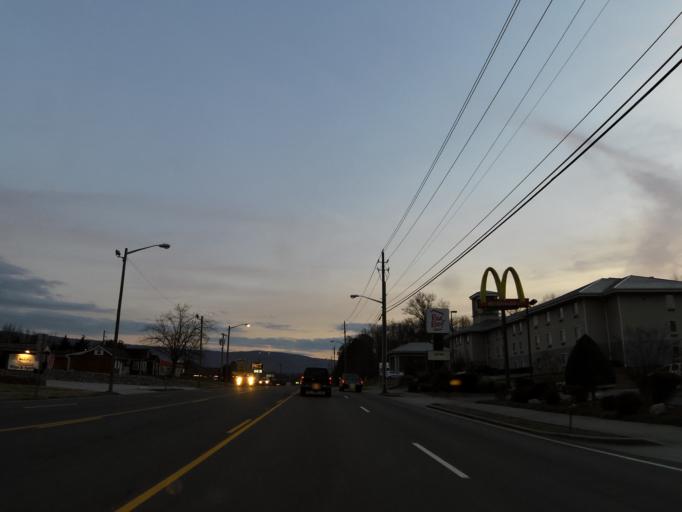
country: US
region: Tennessee
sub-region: McMinn County
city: Etowah
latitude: 35.3392
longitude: -84.5204
